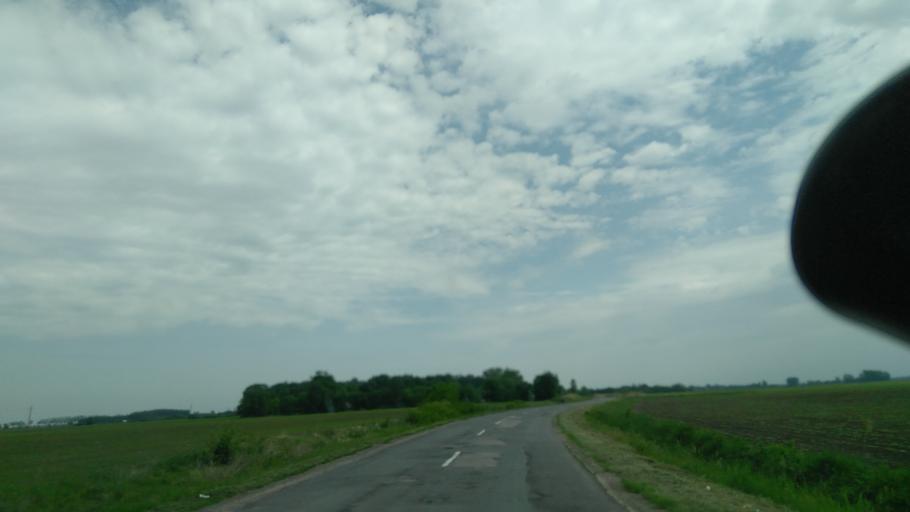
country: HU
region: Hajdu-Bihar
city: Komadi
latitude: 47.0178
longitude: 21.5256
